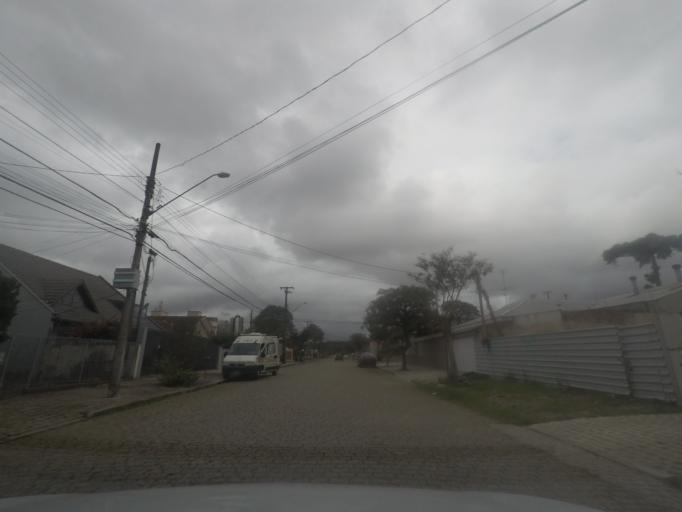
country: BR
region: Parana
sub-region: Curitiba
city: Curitiba
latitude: -25.4396
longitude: -49.2447
